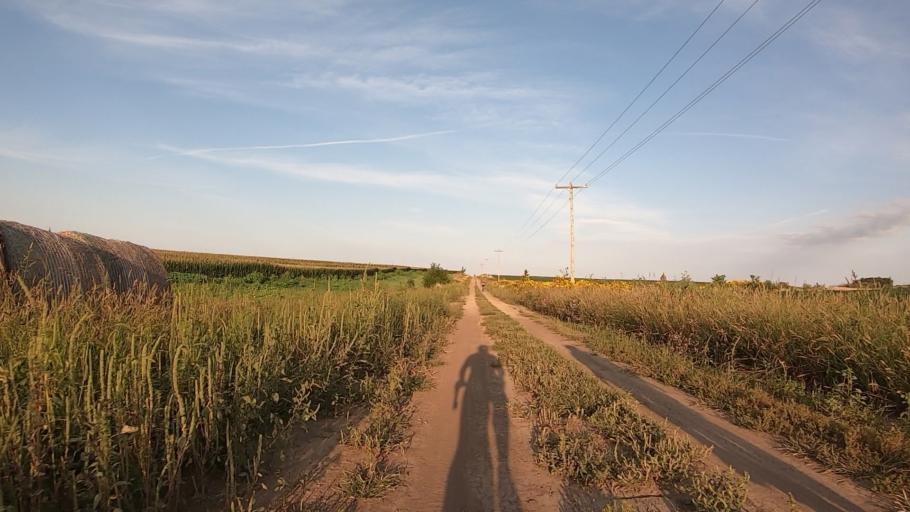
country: US
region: Kansas
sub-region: Marshall County
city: Marysville
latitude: 39.7692
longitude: -96.7281
